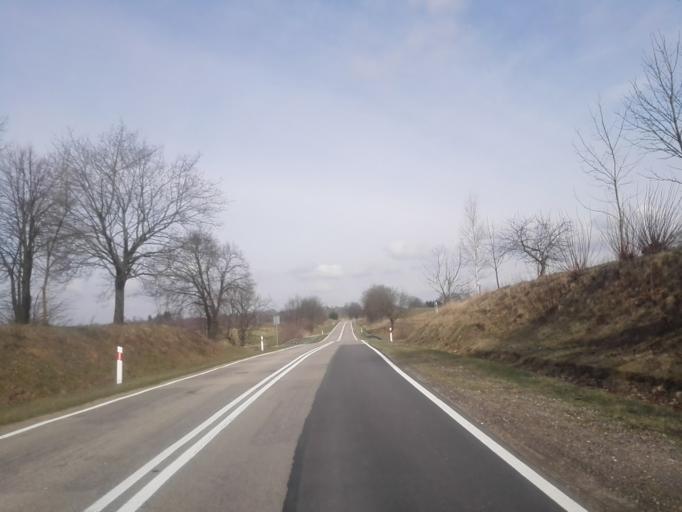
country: PL
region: Podlasie
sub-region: Powiat sejnenski
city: Sejny
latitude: 54.0511
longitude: 23.3549
